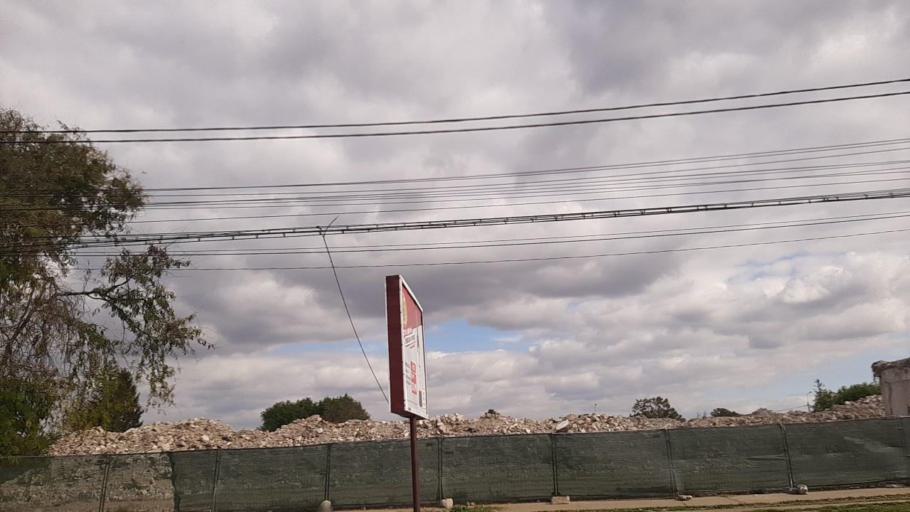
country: RO
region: Galati
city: Galati
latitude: 45.4507
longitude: 28.0349
